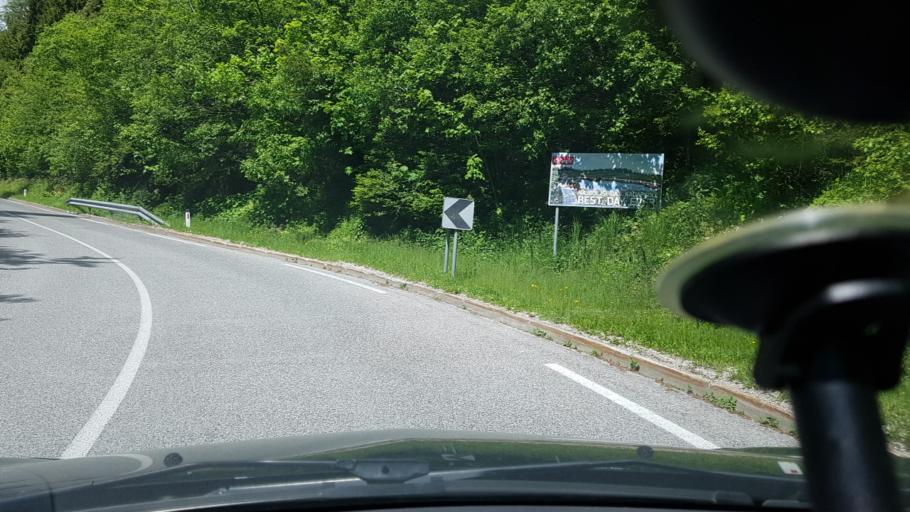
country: SI
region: Zrece
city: Zrece
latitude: 46.4446
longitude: 15.3582
